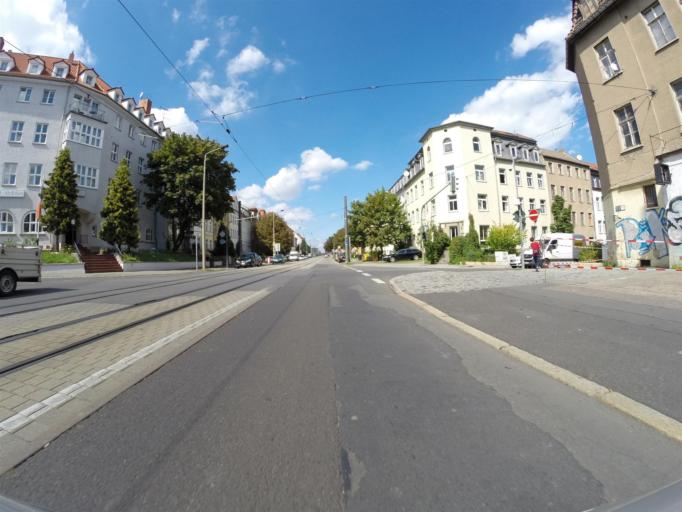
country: DE
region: Thuringia
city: Erfurt
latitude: 50.9844
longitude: 11.0188
